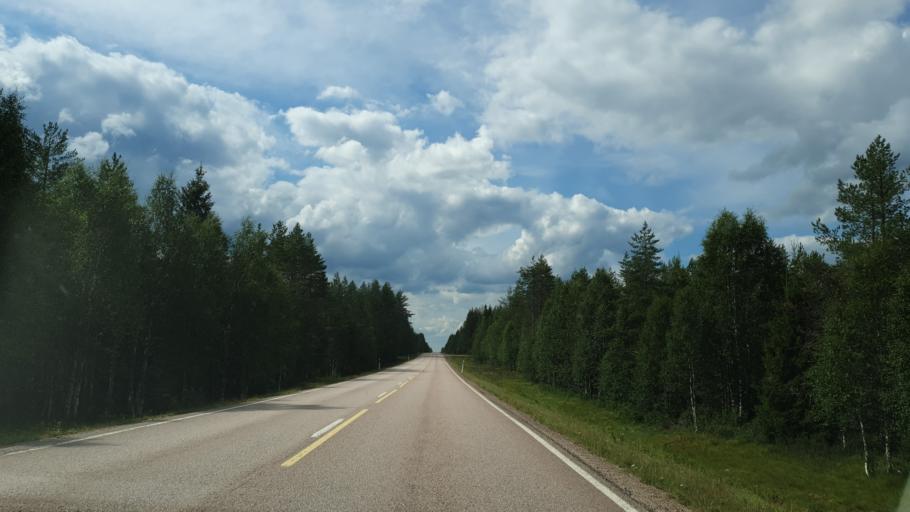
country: FI
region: Kainuu
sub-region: Kehys-Kainuu
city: Hyrynsalmi
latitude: 64.4542
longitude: 28.6707
